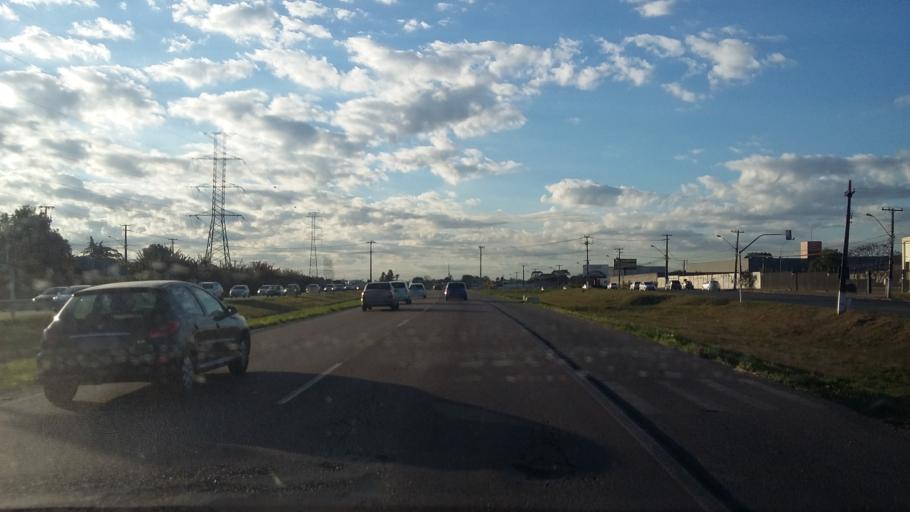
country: BR
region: Parana
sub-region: Curitiba
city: Curitiba
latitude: -25.4960
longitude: -49.3428
